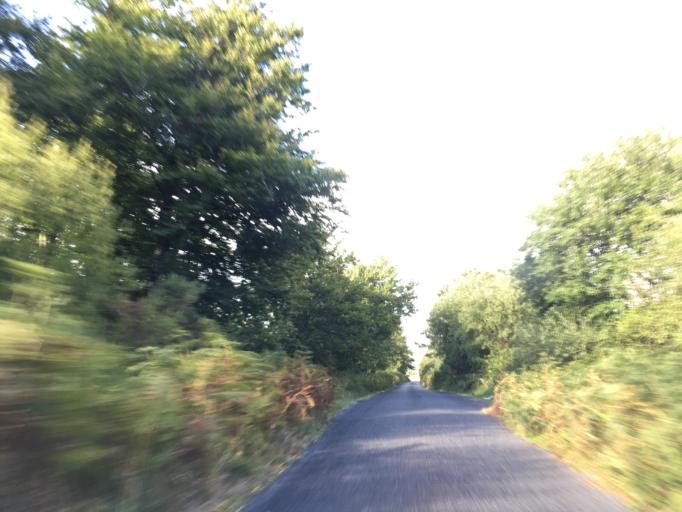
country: IE
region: Munster
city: Cahir
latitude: 52.2646
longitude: -7.9604
